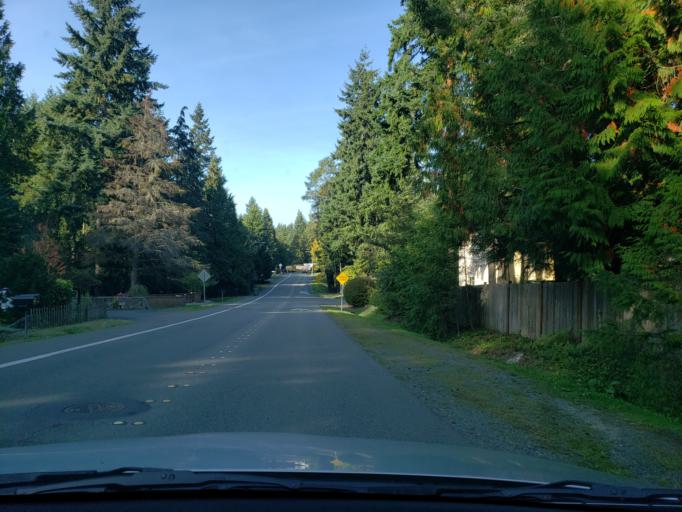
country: US
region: Washington
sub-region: Snohomish County
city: Meadowdale
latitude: 47.8649
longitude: -122.3145
